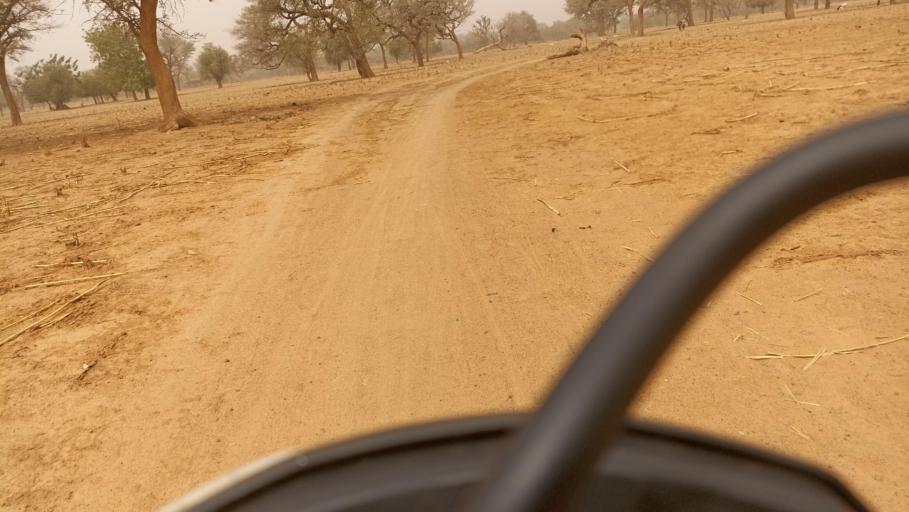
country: BF
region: Nord
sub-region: Province du Zondoma
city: Gourcy
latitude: 13.2493
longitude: -2.5983
